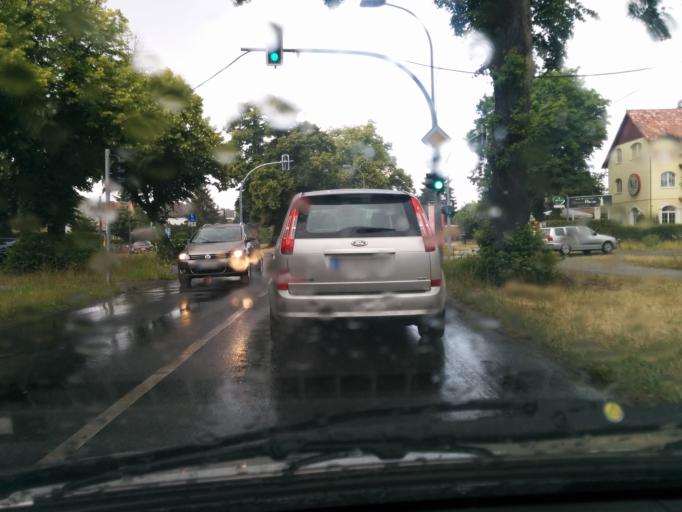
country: DE
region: Berlin
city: Staaken
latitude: 52.5557
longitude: 13.1439
